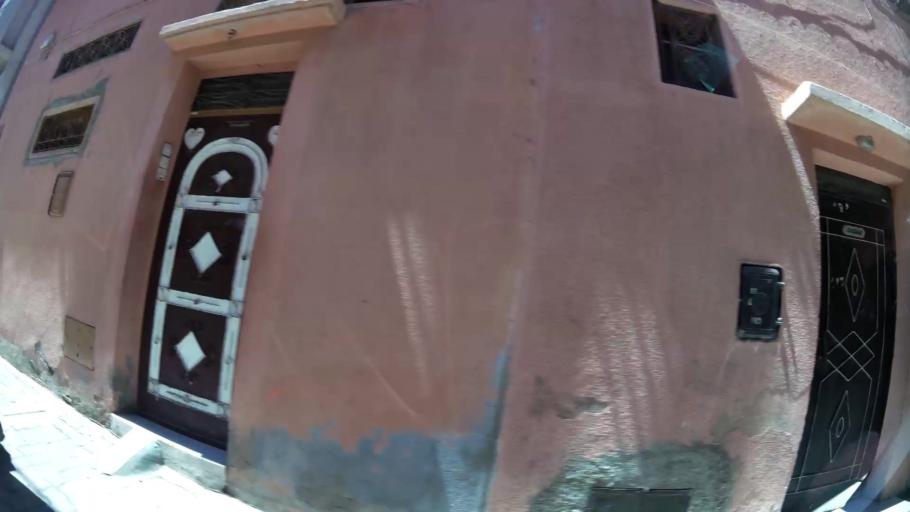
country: MA
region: Marrakech-Tensift-Al Haouz
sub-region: Marrakech
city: Marrakesh
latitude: 31.6369
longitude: -8.0557
